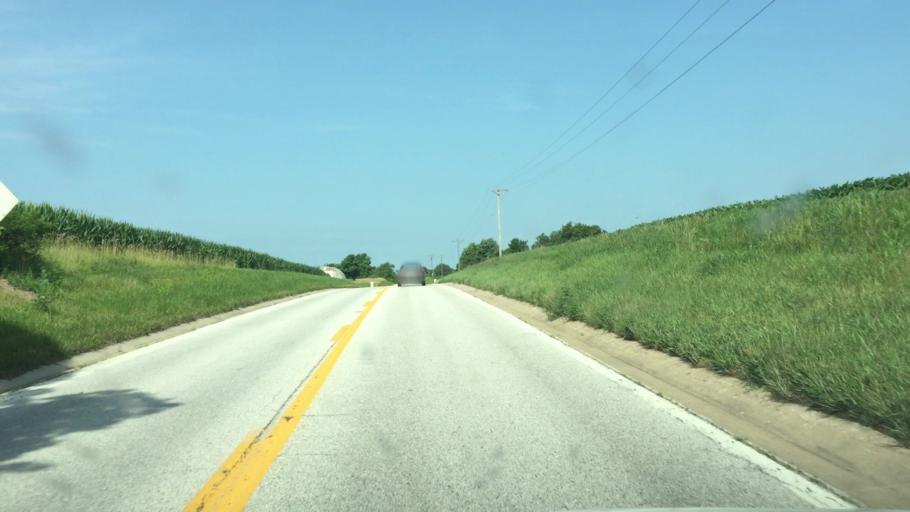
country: US
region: Illinois
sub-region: Hancock County
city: Nauvoo
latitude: 40.5516
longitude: -91.3177
